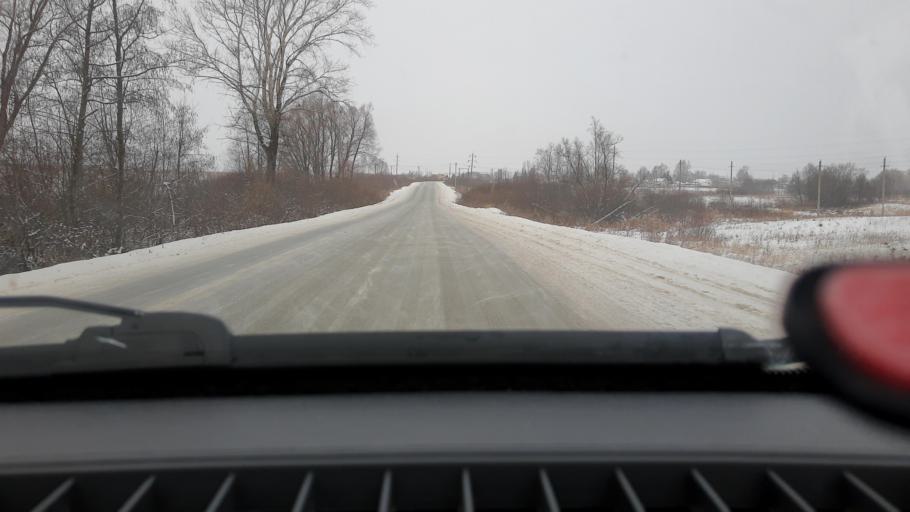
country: RU
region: Bashkortostan
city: Iglino
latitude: 54.7295
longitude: 56.4018
